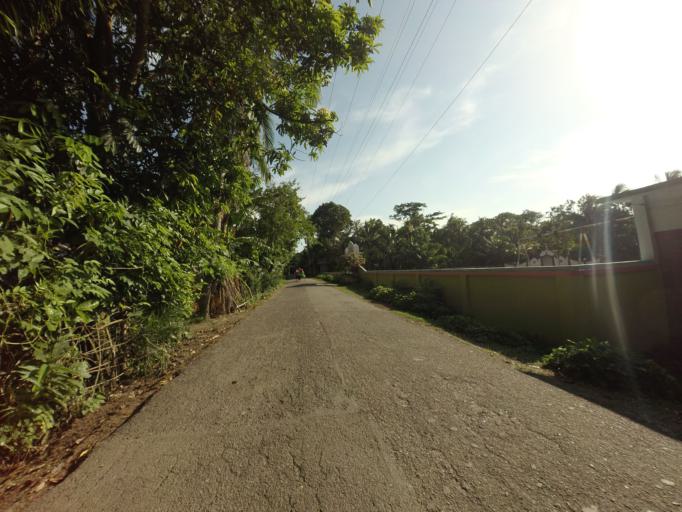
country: BD
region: Khulna
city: Kalia
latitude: 23.0098
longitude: 89.5852
